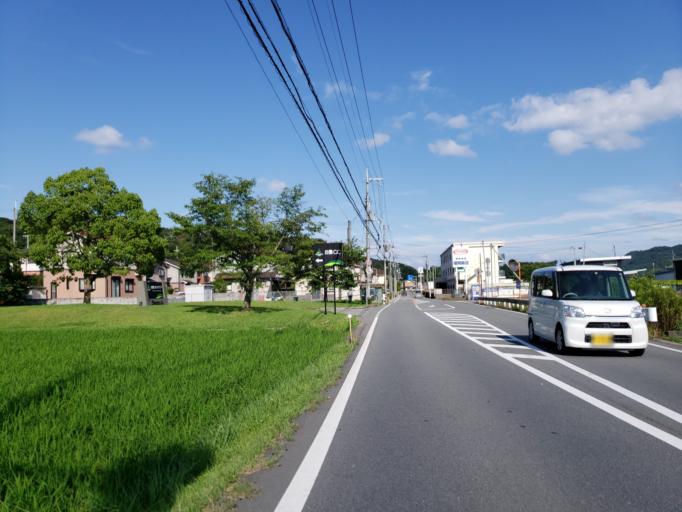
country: JP
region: Hyogo
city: Himeji
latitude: 34.9063
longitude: 134.7902
